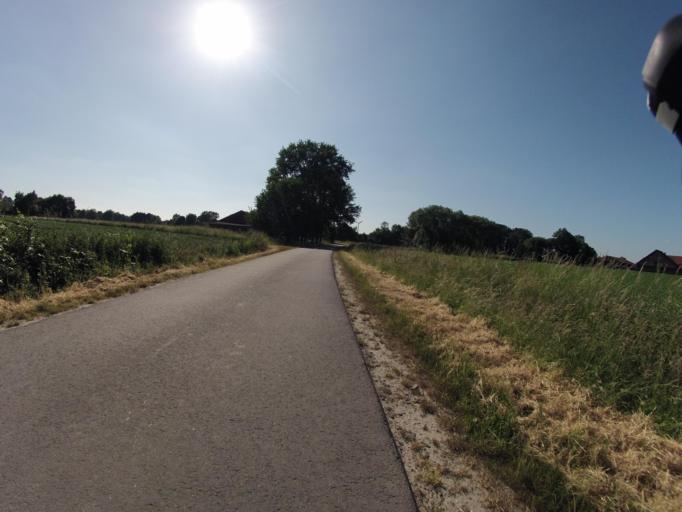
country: DE
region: Lower Saxony
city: Salzbergen
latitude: 52.3089
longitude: 7.3826
